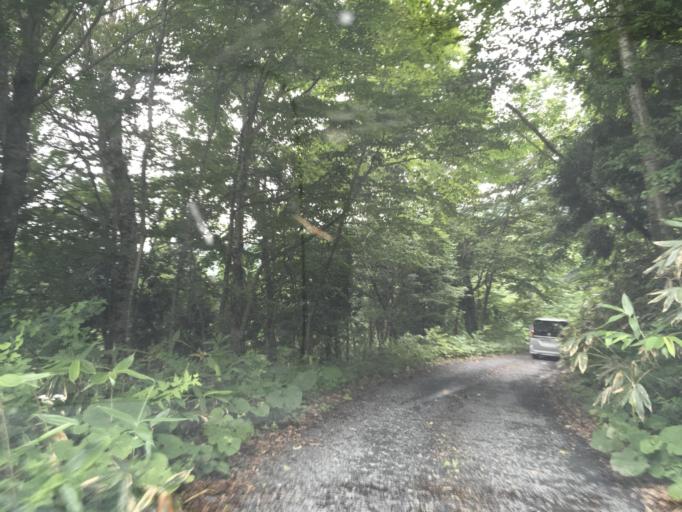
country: JP
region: Iwate
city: Ichinoseki
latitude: 38.9524
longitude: 140.8524
